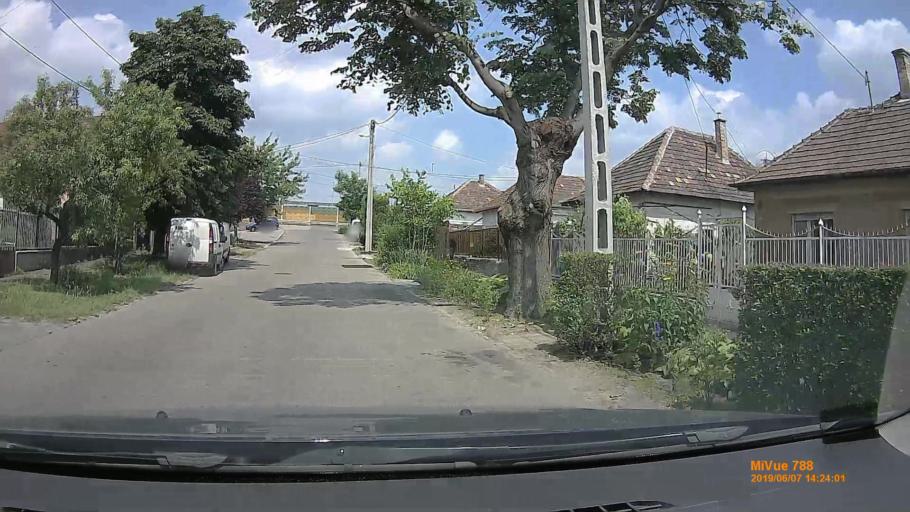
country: HU
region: Budapest
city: Budapest XIX. keruelet
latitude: 47.4361
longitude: 19.1420
